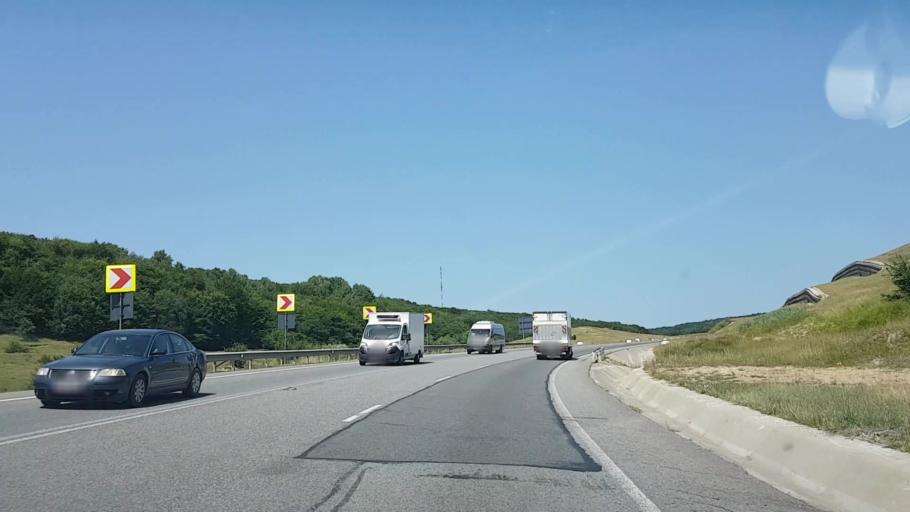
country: RO
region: Cluj
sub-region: Comuna Feleacu
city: Feleacu
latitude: 46.6957
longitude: 23.6359
